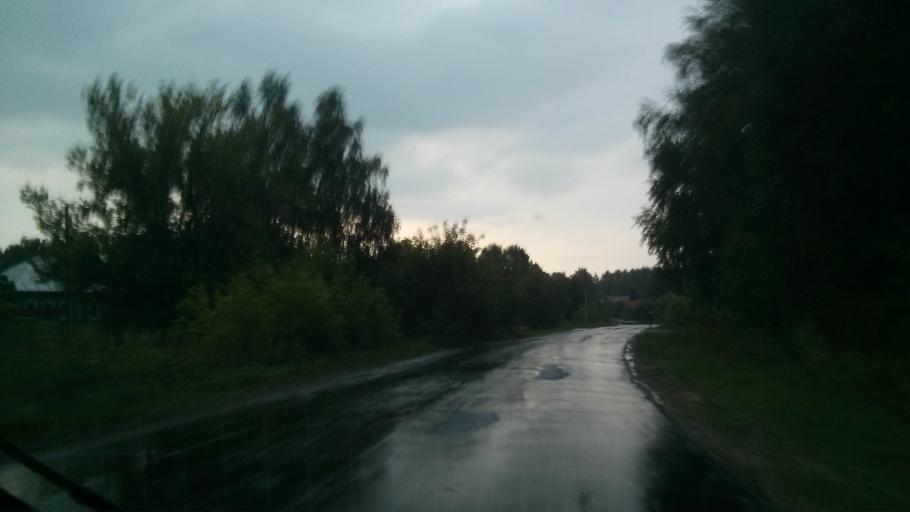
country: RU
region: Nizjnij Novgorod
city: Shimorskoye
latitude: 55.3444
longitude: 41.9294
